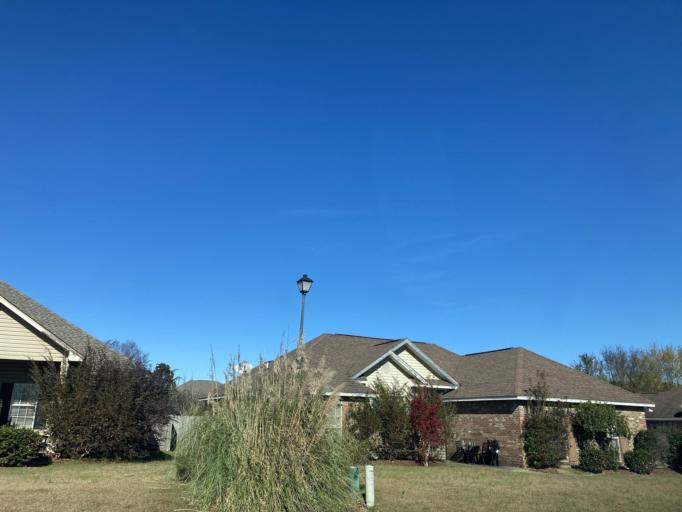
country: US
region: Mississippi
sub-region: Forrest County
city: Petal
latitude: 31.3220
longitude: -89.1861
